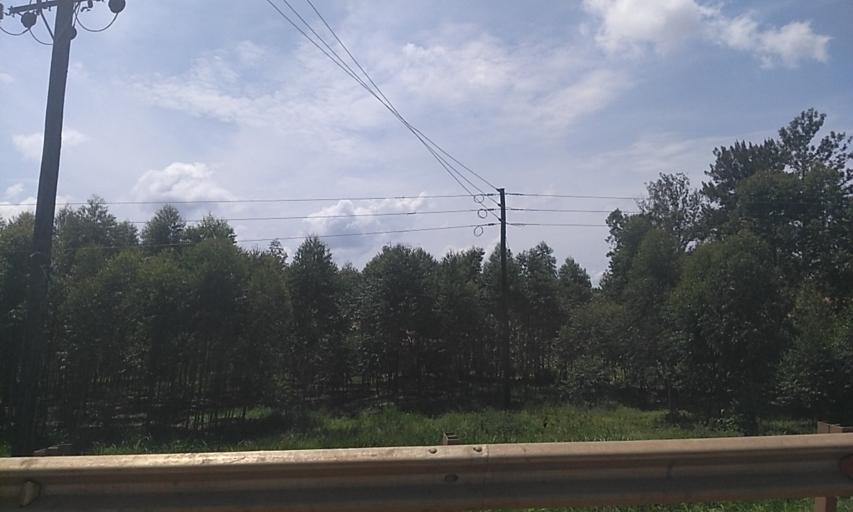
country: UG
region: Central Region
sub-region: Wakiso District
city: Wakiso
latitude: 0.3880
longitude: 32.5113
